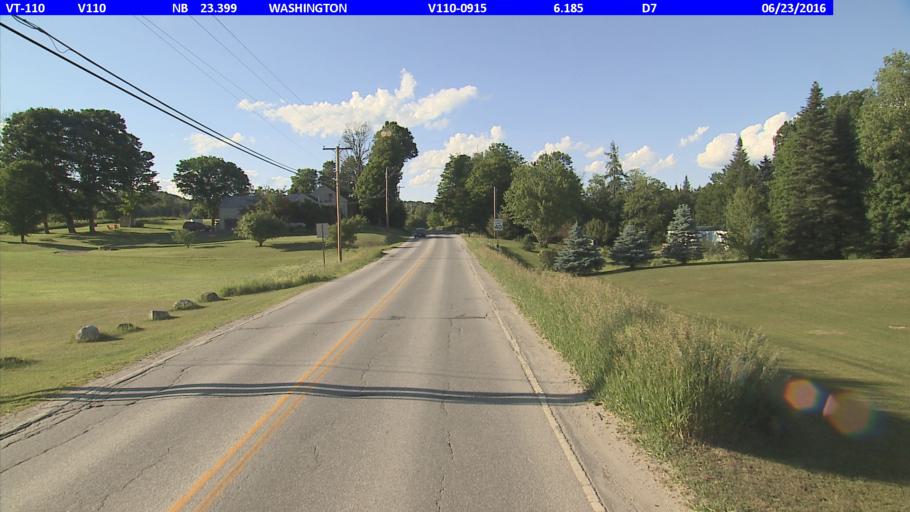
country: US
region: Vermont
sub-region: Washington County
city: South Barre
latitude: 44.1125
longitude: -72.4337
